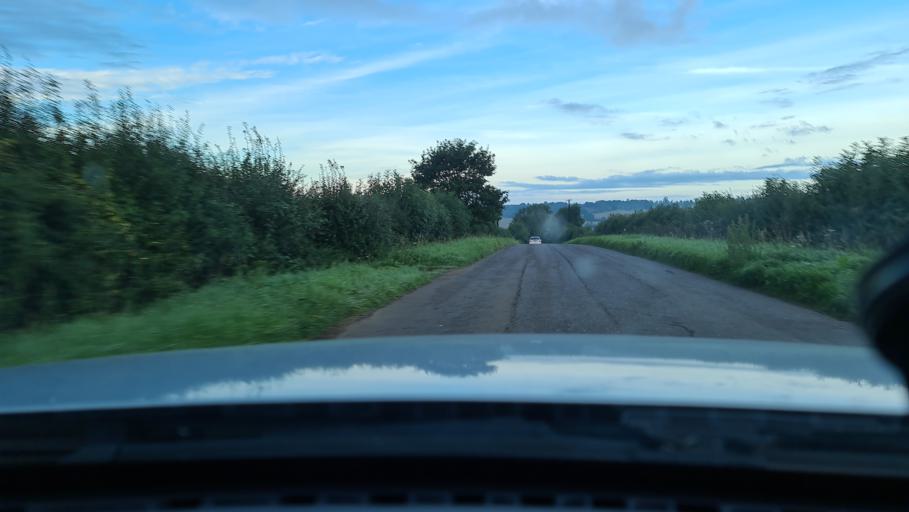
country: GB
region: England
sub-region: Oxfordshire
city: Hanwell
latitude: 52.1009
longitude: -1.3448
